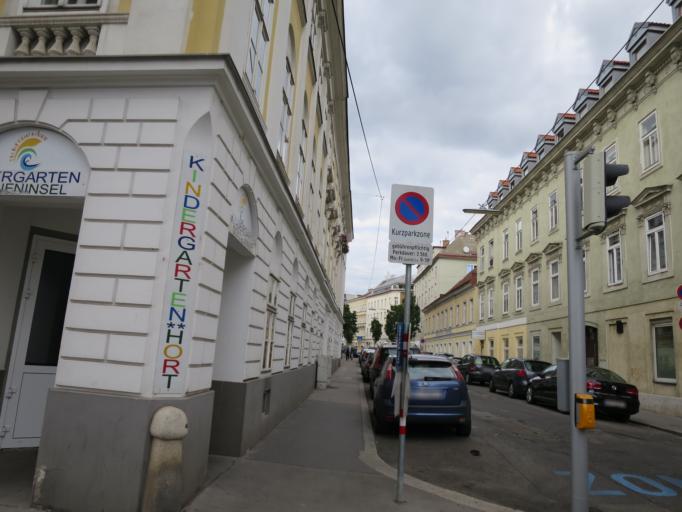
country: AT
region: Vienna
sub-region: Wien Stadt
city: Vienna
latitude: 48.2115
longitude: 16.3335
